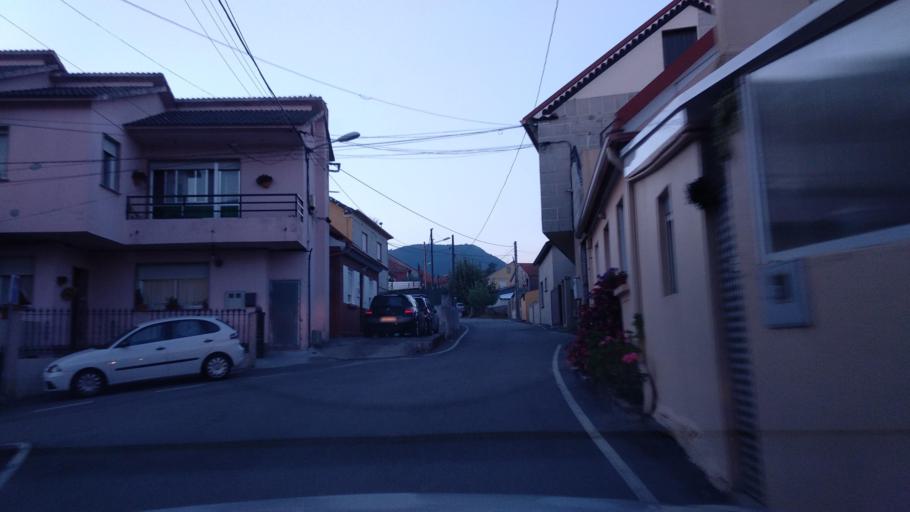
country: ES
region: Galicia
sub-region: Provincia de Pontevedra
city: Moana
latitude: 42.2885
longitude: -8.7267
